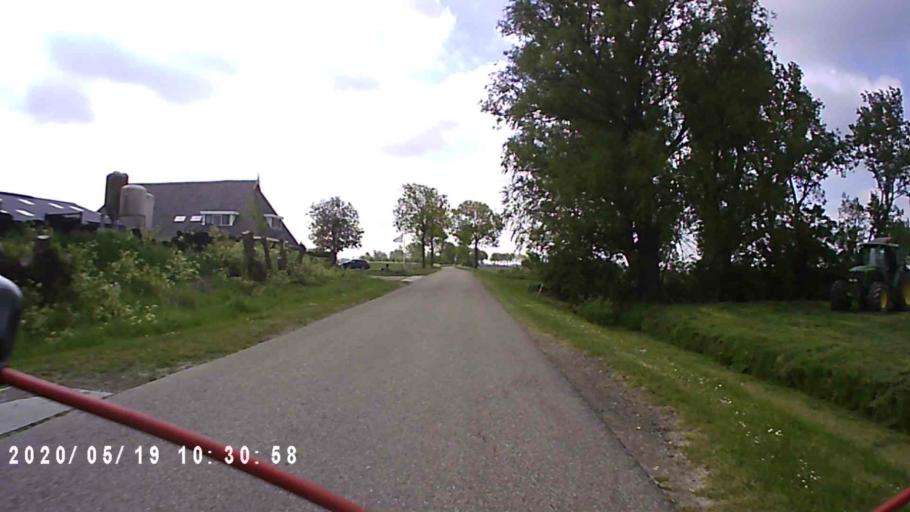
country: NL
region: Friesland
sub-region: Gemeente Kollumerland en Nieuwkruisland
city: Kollum
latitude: 53.2929
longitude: 6.1960
